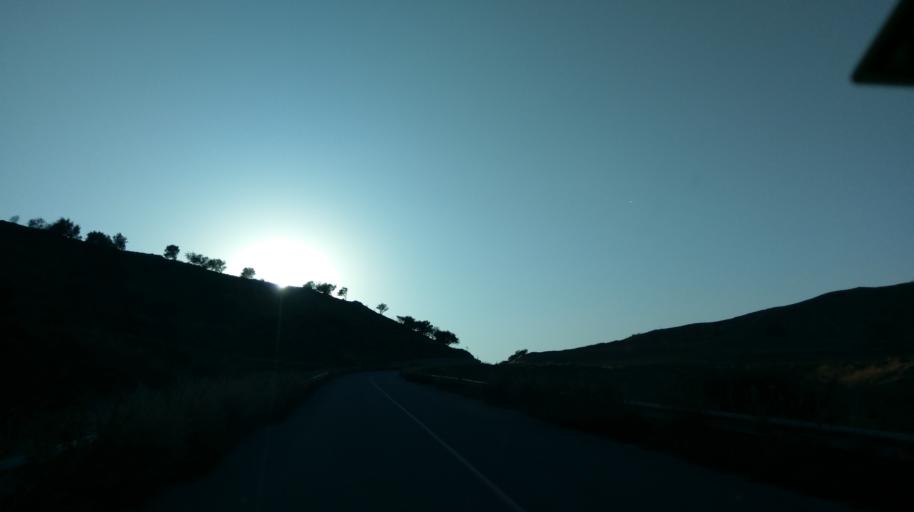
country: CY
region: Ammochostos
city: Trikomo
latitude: 35.3681
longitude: 33.9459
